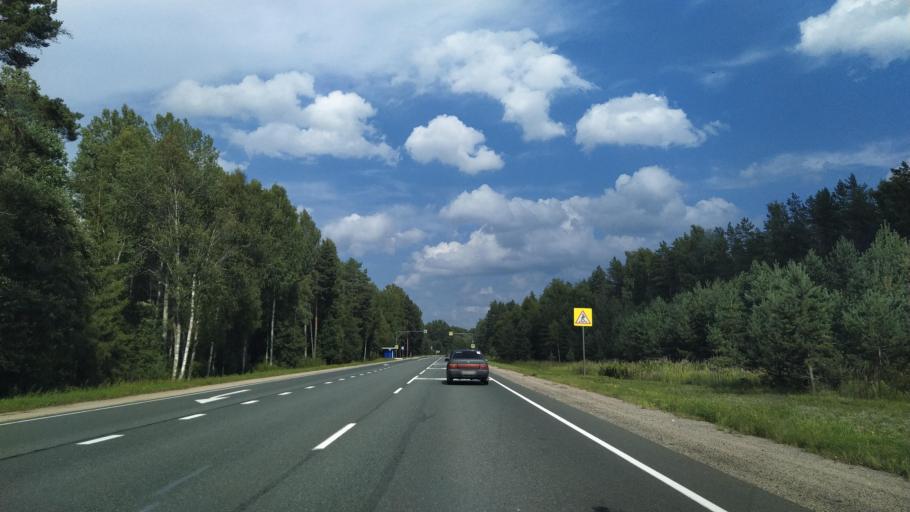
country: RU
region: Pskov
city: Porkhov
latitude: 57.8610
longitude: 29.5728
